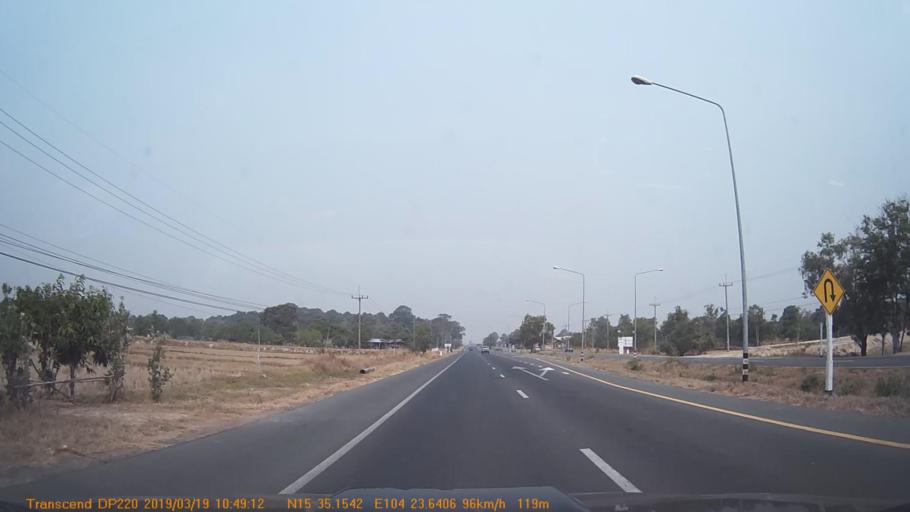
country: TH
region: Yasothon
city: Kham Khuean Kaeo
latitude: 15.5861
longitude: 104.3939
